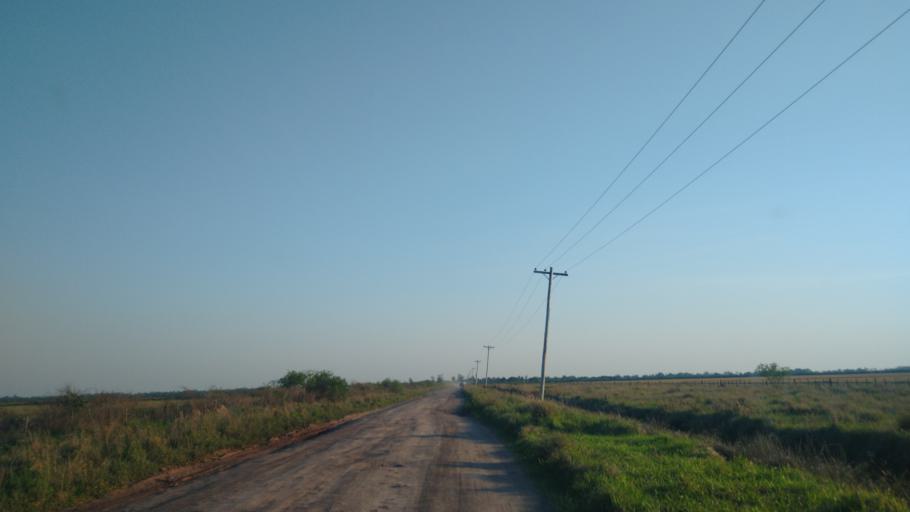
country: PY
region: Neembucu
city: Cerrito
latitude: -27.3885
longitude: -57.6581
